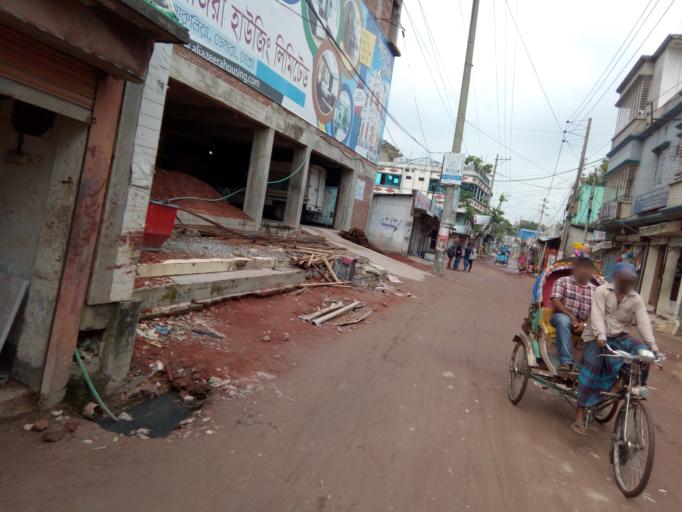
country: BD
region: Dhaka
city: Paltan
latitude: 23.7115
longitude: 90.4912
